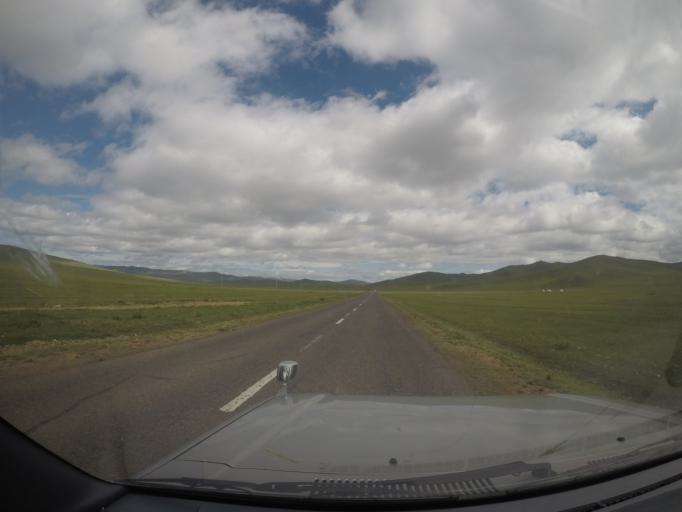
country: MN
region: Hentiy
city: Modot
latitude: 47.7647
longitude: 108.9008
